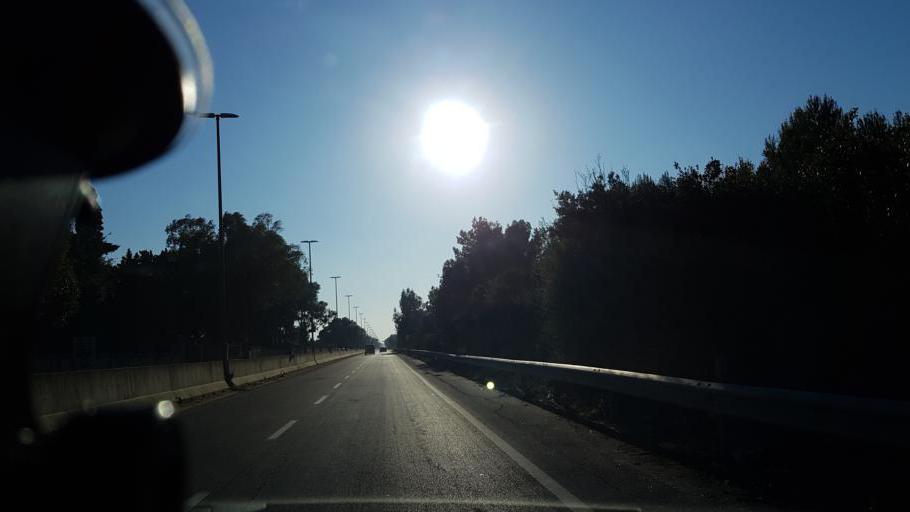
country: IT
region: Apulia
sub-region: Provincia di Lecce
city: Struda
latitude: 40.3875
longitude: 18.2960
